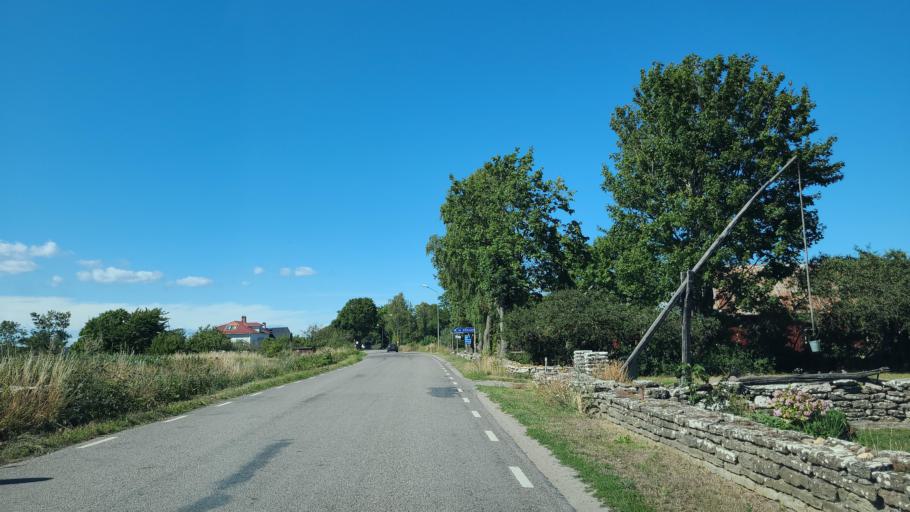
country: SE
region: Kalmar
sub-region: Borgholms Kommun
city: Borgholm
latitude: 56.7810
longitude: 16.7395
